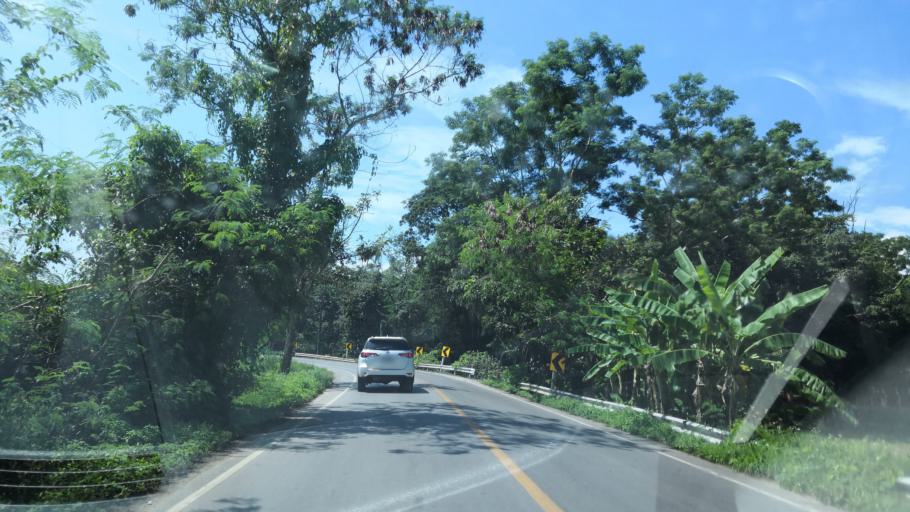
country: TH
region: Chiang Rai
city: Wiang Chai
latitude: 19.9706
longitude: 99.9669
